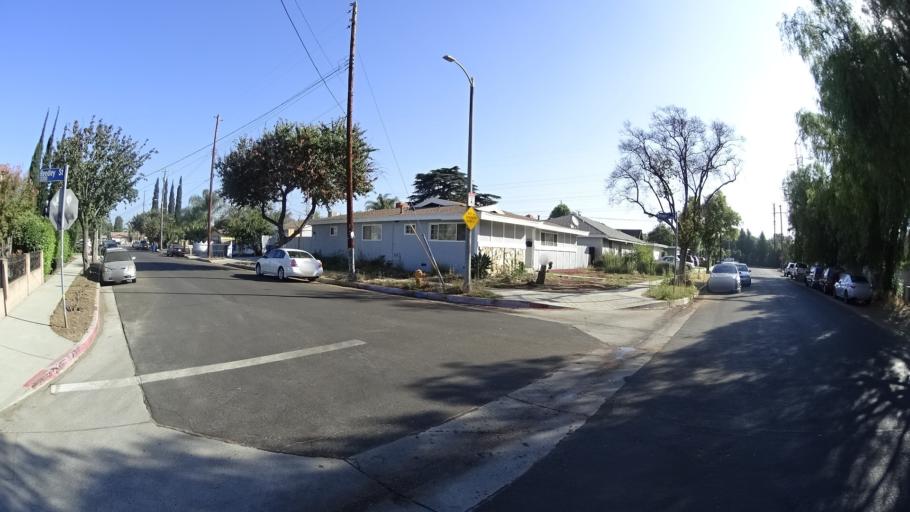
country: US
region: California
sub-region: Los Angeles County
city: Van Nuys
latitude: 34.2265
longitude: -118.4220
